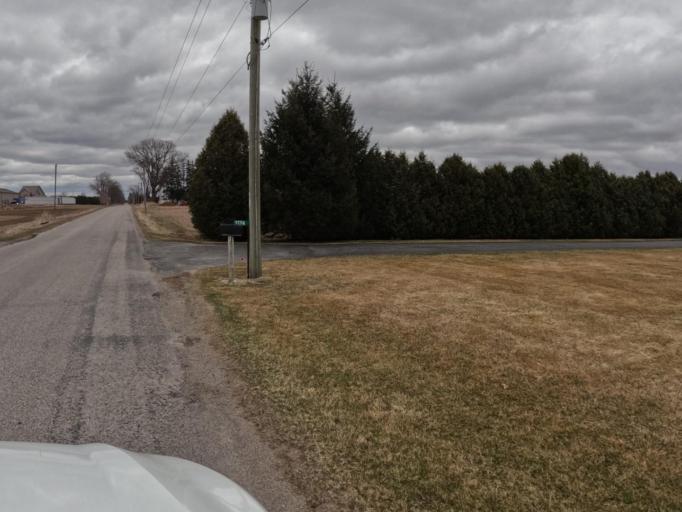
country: CA
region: Ontario
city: Norfolk County
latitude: 42.9418
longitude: -80.4126
